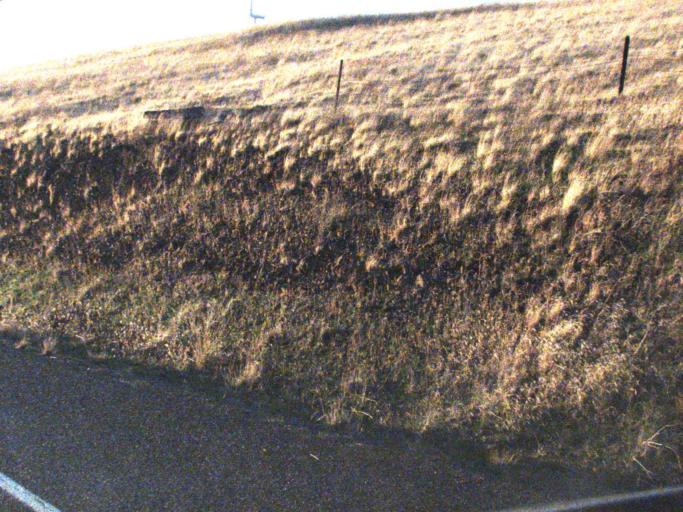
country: US
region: Washington
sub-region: Garfield County
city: Pomeroy
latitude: 46.5254
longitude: -117.7981
